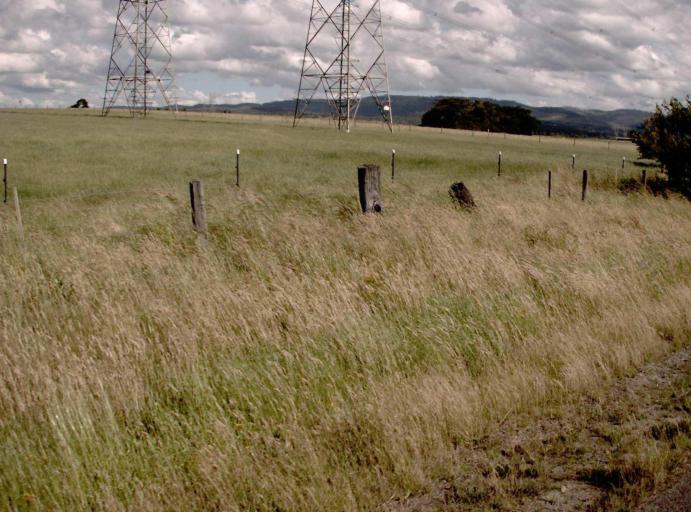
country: AU
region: Victoria
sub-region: Latrobe
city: Morwell
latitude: -38.2707
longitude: 146.4336
